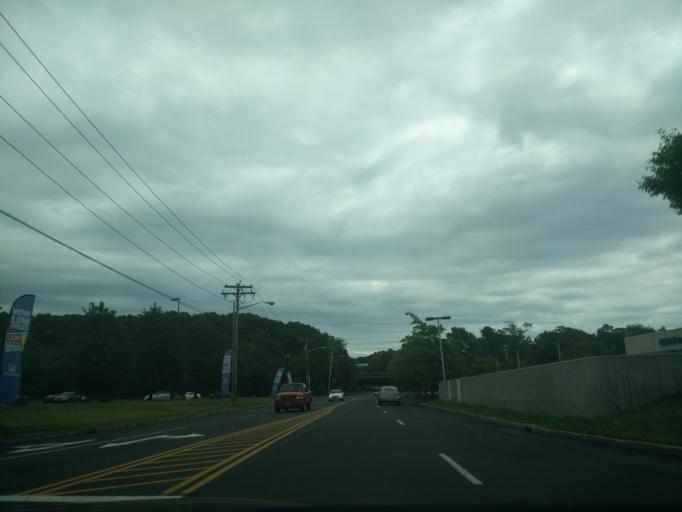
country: US
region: Connecticut
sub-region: New Haven County
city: Milford
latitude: 41.2365
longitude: -73.0321
